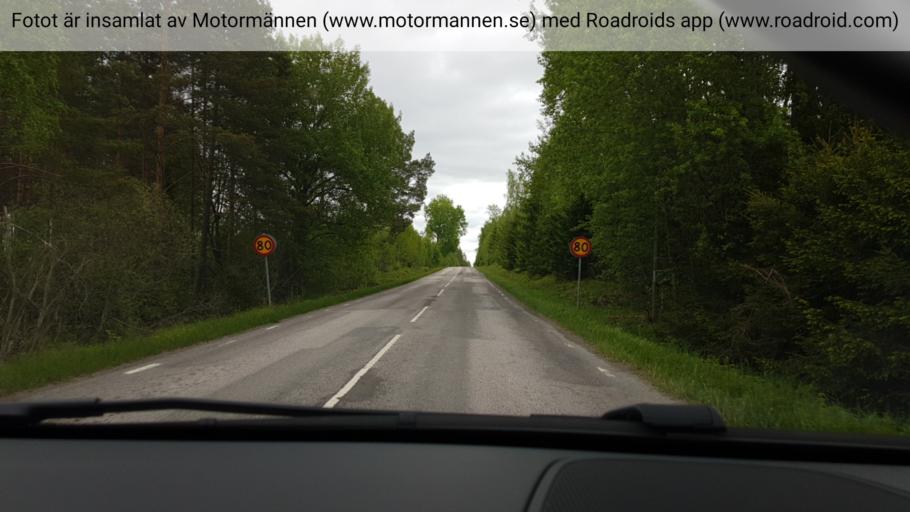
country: SE
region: Uppsala
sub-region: Heby Kommun
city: Tarnsjo
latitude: 60.1503
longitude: 16.9519
